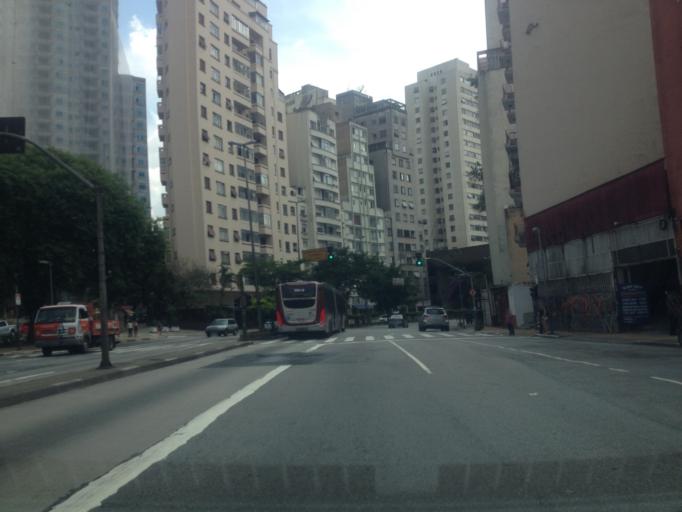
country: BR
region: Sao Paulo
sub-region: Sao Paulo
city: Sao Paulo
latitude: -23.5524
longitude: -46.6474
